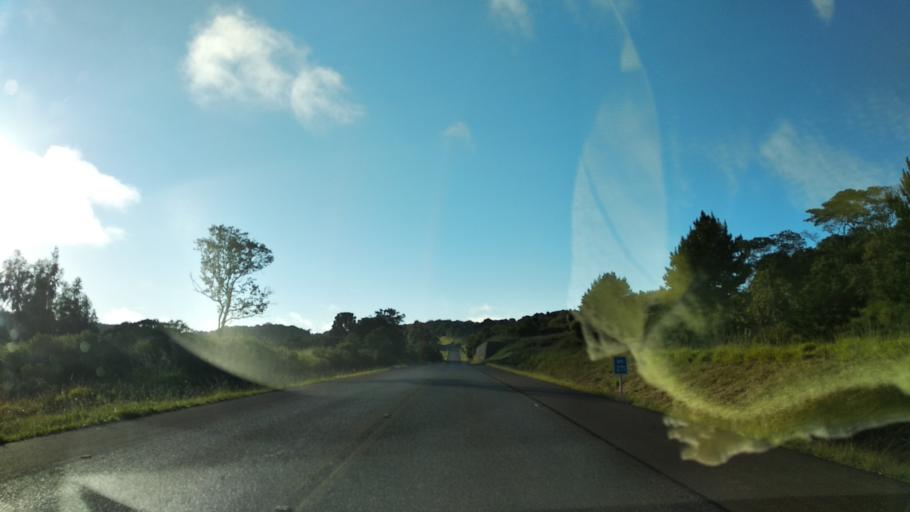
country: BR
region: Santa Catarina
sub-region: Correia Pinto
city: Correia Pinto
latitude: -27.6146
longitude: -50.6905
